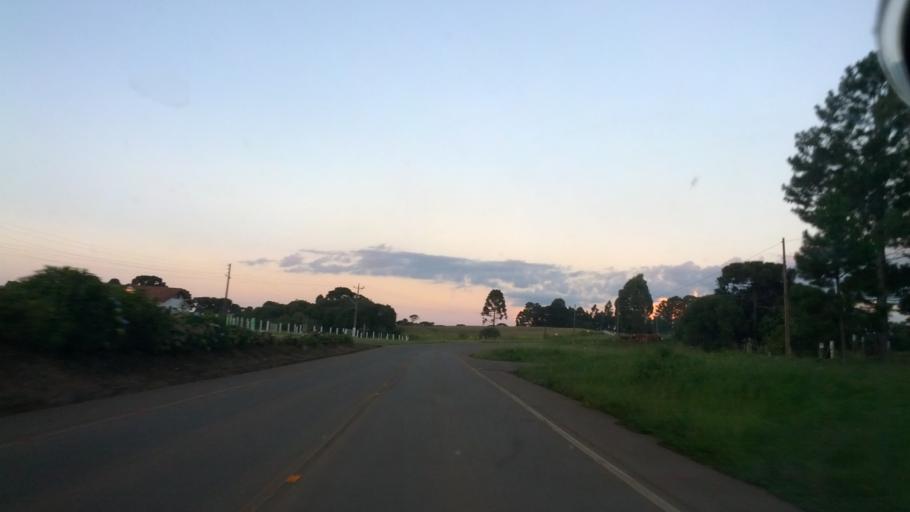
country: BR
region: Rio Grande do Sul
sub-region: Vacaria
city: Estrela
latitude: -27.8993
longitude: -50.7779
